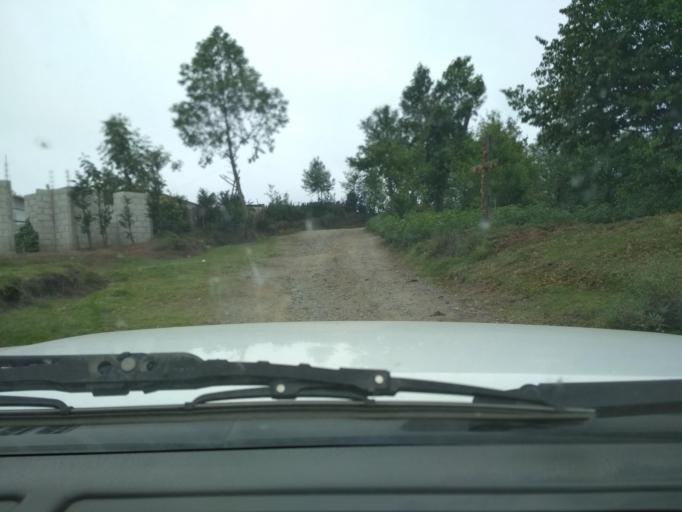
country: MX
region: Veracruz
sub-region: La Perla
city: Chilapa
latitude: 18.9945
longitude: -97.1678
